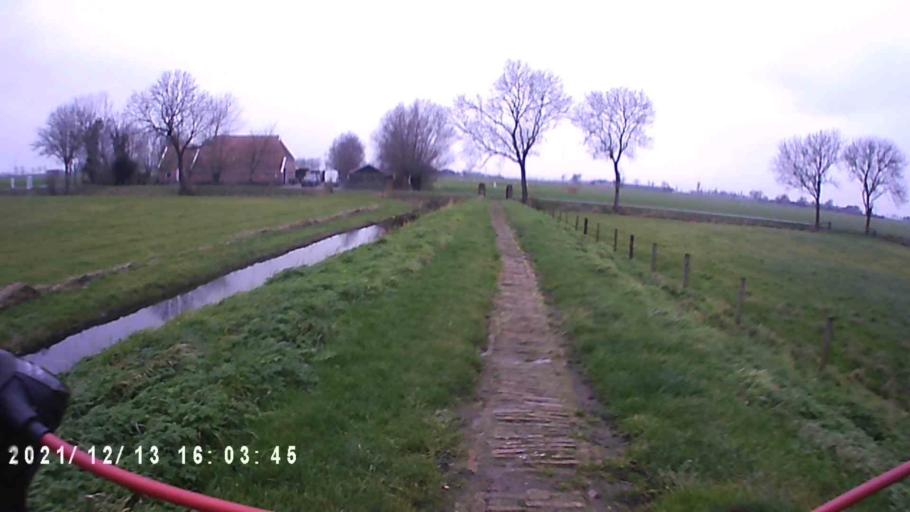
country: NL
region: Groningen
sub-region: Gemeente Appingedam
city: Appingedam
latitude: 53.3398
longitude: 6.8745
